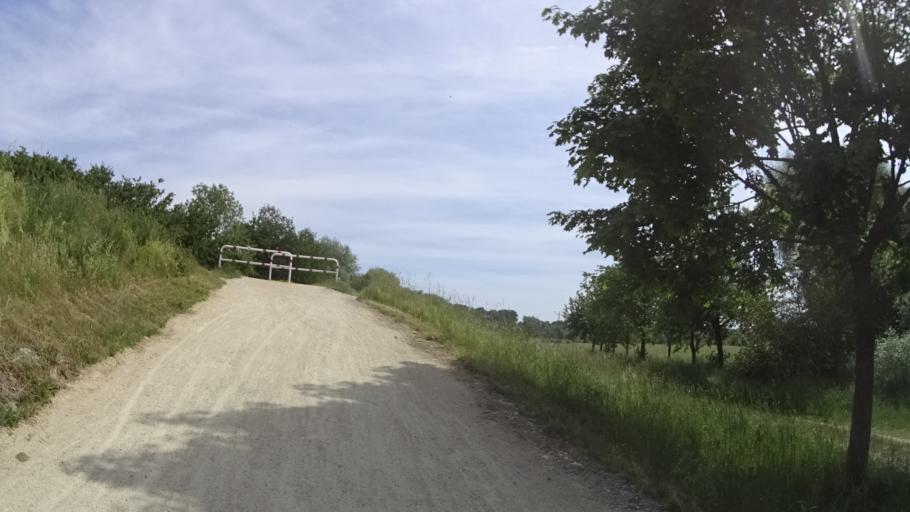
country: DE
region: Bavaria
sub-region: Lower Bavaria
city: Saal
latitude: 48.9119
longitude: 11.9156
